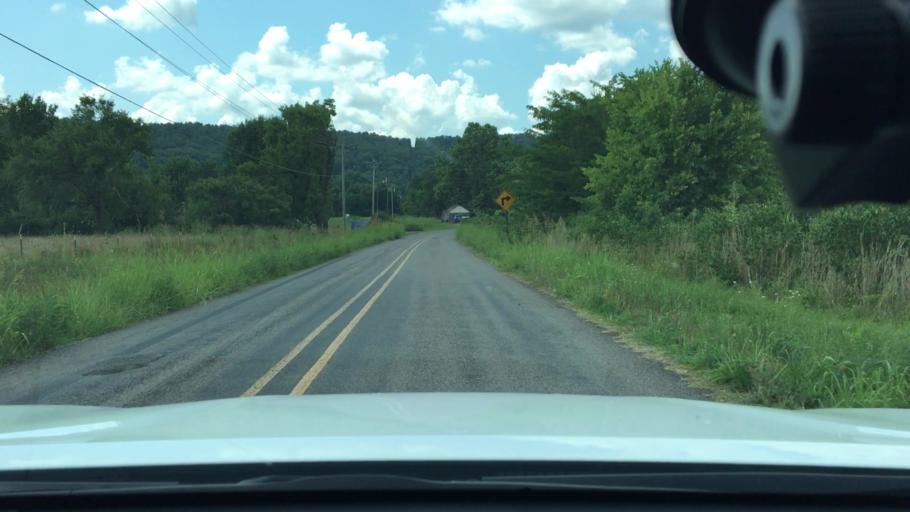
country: US
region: Arkansas
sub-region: Logan County
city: Paris
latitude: 35.2701
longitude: -93.6516
